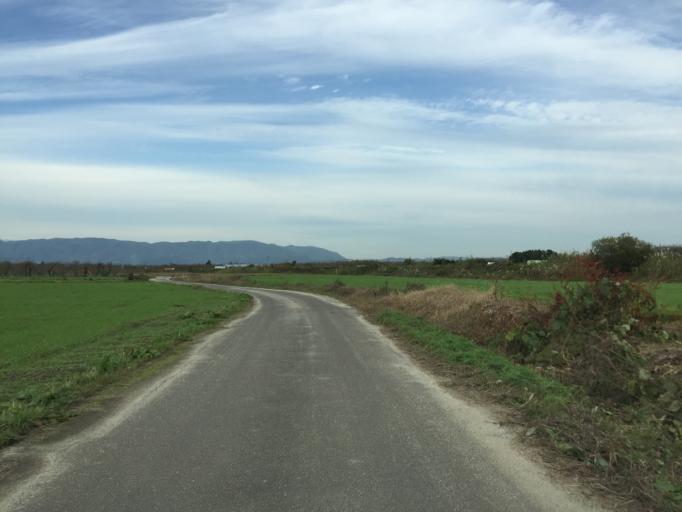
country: JP
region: Fukushima
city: Hobaramachi
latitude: 37.8164
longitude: 140.5315
